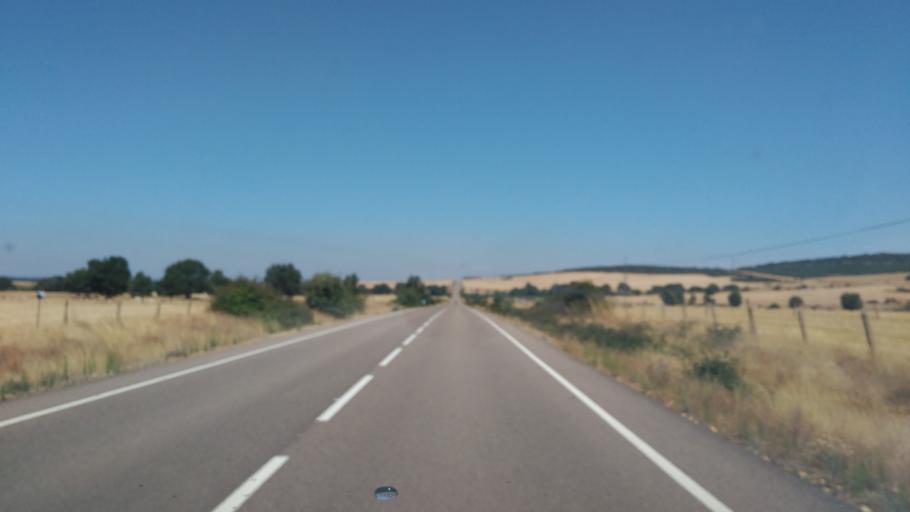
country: ES
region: Castille and Leon
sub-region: Provincia de Salamanca
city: Tamames
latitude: 40.6368
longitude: -6.1108
